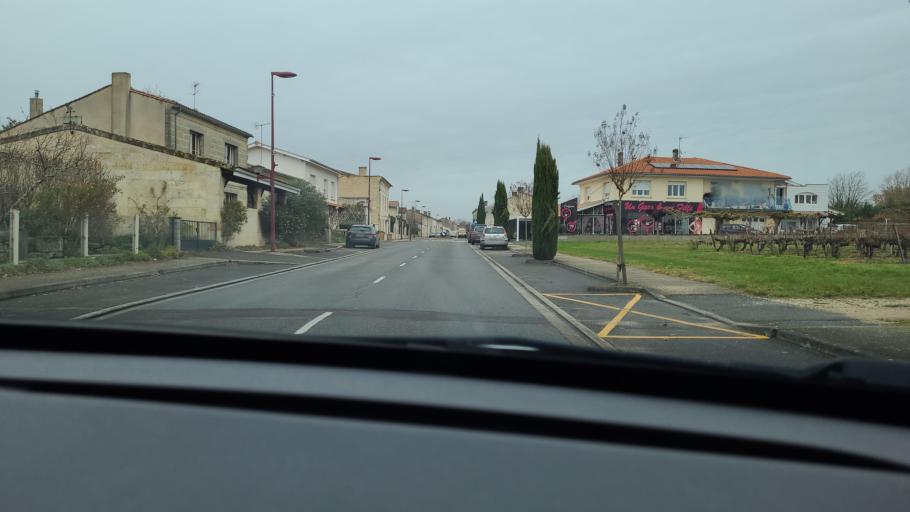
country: FR
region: Aquitaine
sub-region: Departement de la Gironde
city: Pugnac
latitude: 45.0796
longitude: -0.4994
